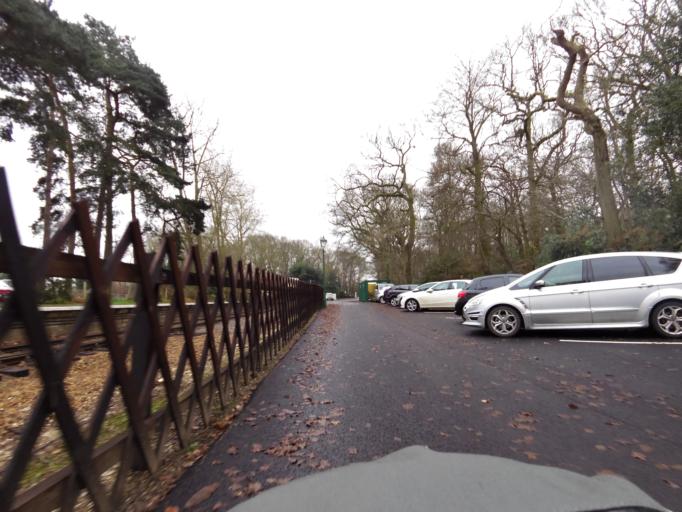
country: GB
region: England
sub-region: Norfolk
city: Briston
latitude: 52.9129
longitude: 1.1133
